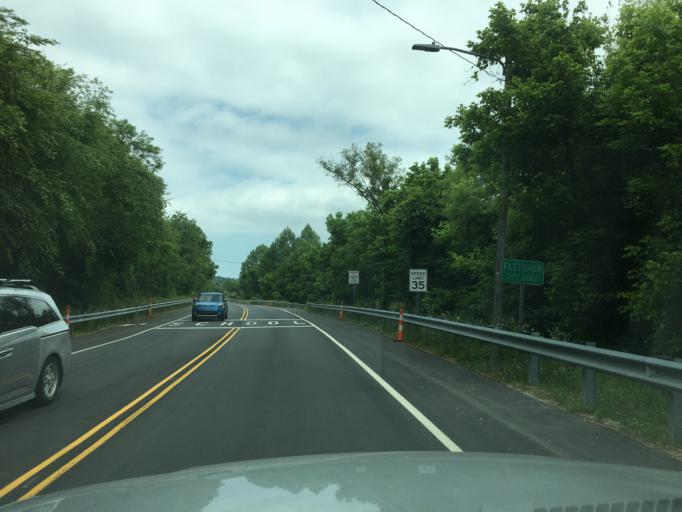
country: US
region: North Carolina
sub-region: Henderson County
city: Fletcher
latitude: 35.4219
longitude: -82.4994
